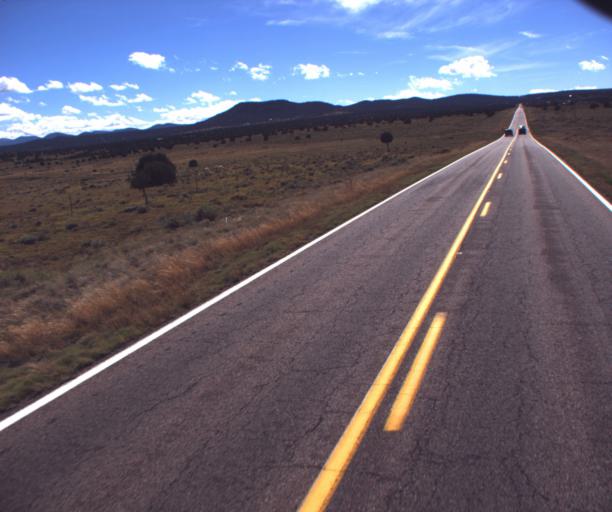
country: US
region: Arizona
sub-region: Navajo County
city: White Mountain Lake
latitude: 34.3481
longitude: -109.7235
